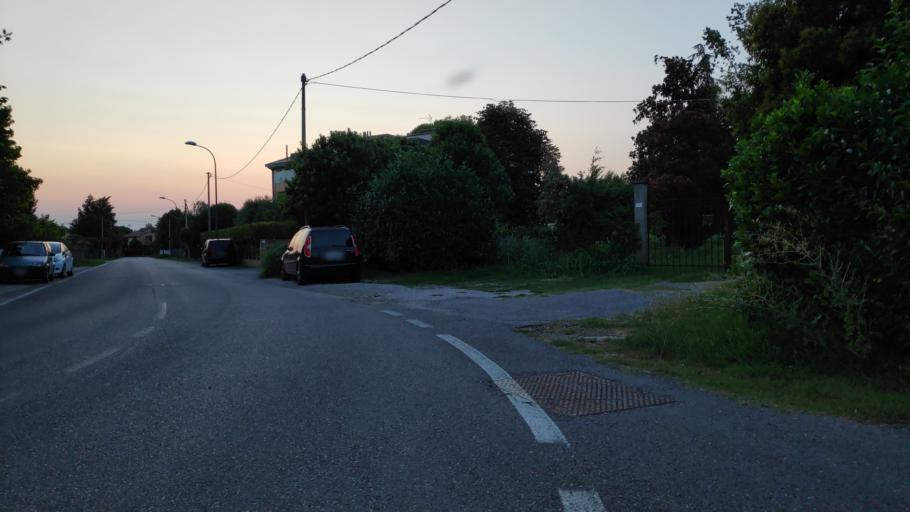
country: IT
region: Veneto
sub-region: Provincia di Treviso
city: Carbonera
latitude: 45.6715
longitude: 12.2669
